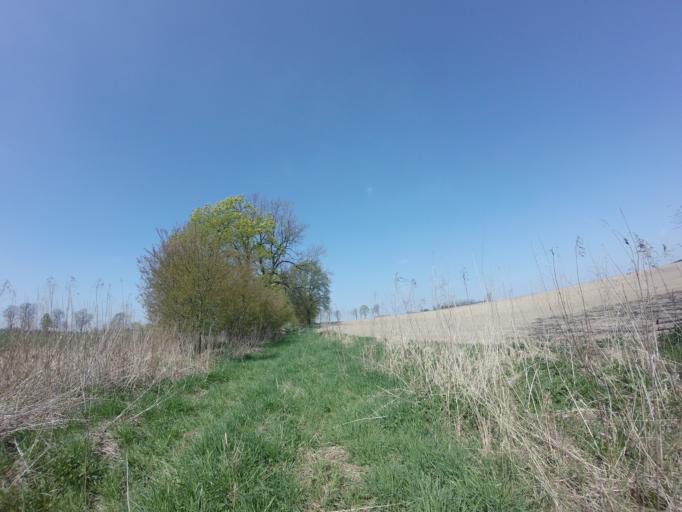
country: PL
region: West Pomeranian Voivodeship
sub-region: Powiat choszczenski
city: Choszczno
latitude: 53.2009
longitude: 15.3694
